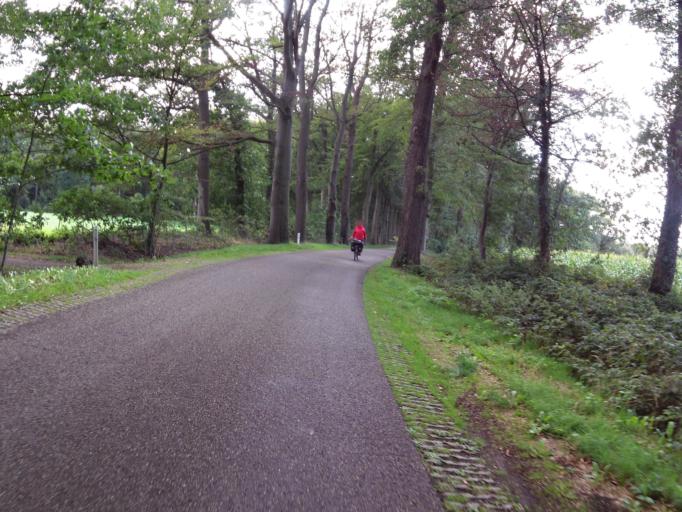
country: NL
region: Gelderland
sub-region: Gemeente Aalten
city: Bredevoort
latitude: 51.9644
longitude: 6.6310
